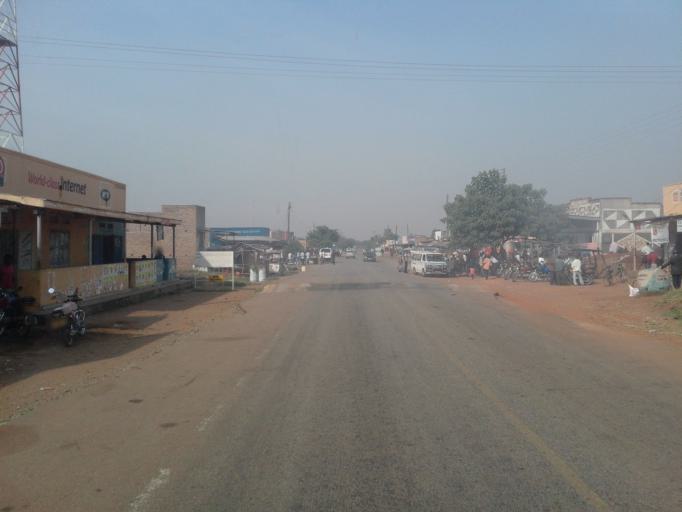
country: UG
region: Eastern Region
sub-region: Budaka District
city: Budaka
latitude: 1.0160
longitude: 33.9498
